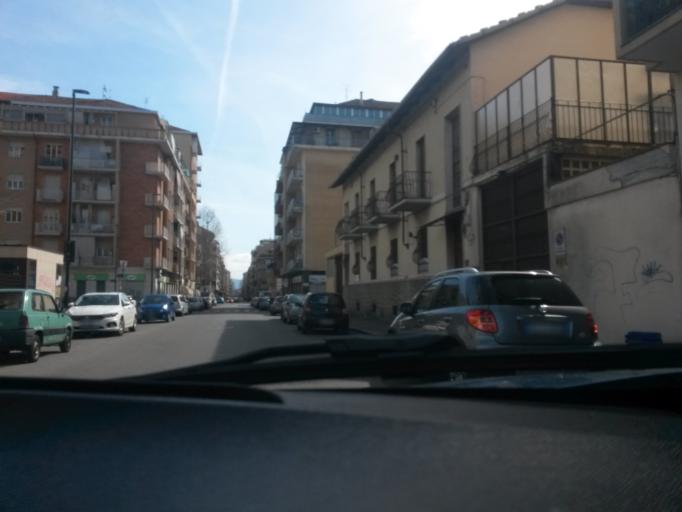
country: IT
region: Piedmont
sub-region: Provincia di Torino
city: Lesna
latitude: 45.0821
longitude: 7.6308
